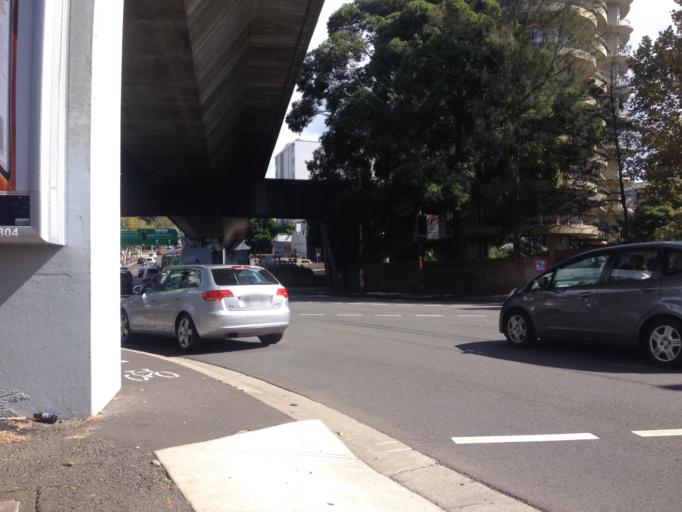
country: AU
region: New South Wales
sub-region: Woollahra
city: Paddington
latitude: -33.8769
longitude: 151.2298
